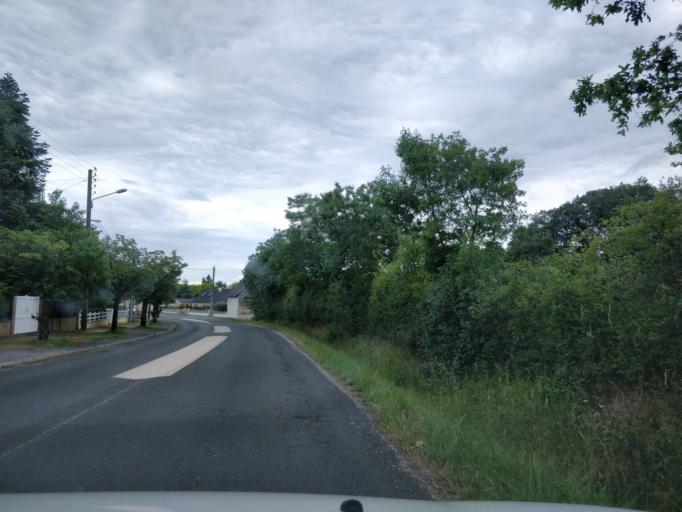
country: FR
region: Pays de la Loire
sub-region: Departement de Maine-et-Loire
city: Feneu
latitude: 47.5748
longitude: -0.5965
